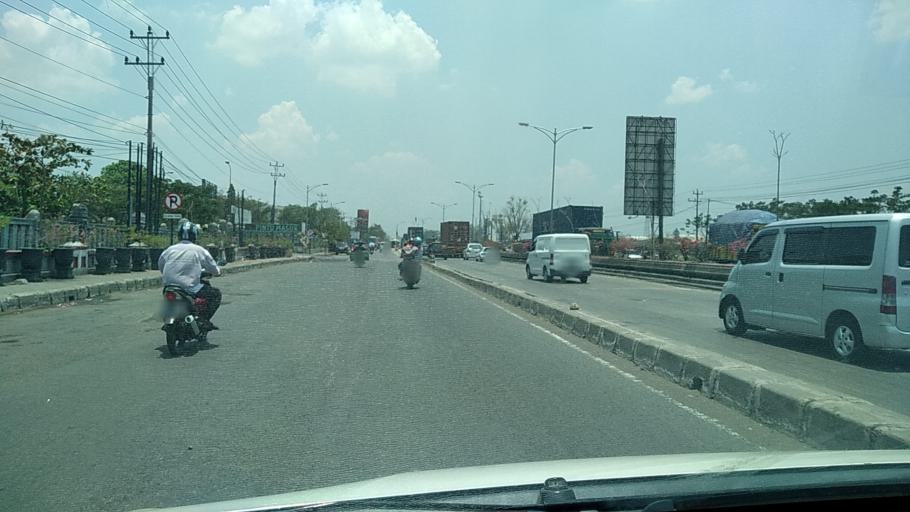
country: ID
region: Central Java
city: Semarang
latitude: -6.9562
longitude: 110.4611
